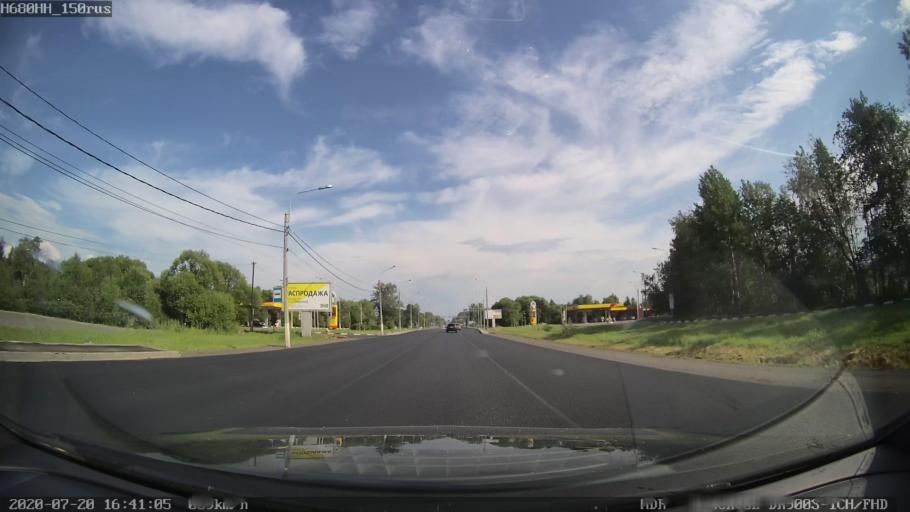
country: RU
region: Leningrad
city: Gorbunki
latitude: 59.8707
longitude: 29.9702
